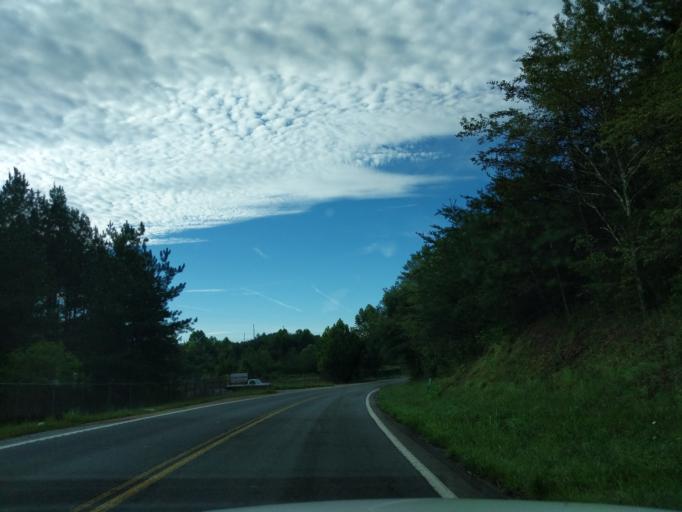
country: US
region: Georgia
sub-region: Fannin County
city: McCaysville
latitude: 34.9983
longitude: -84.3833
